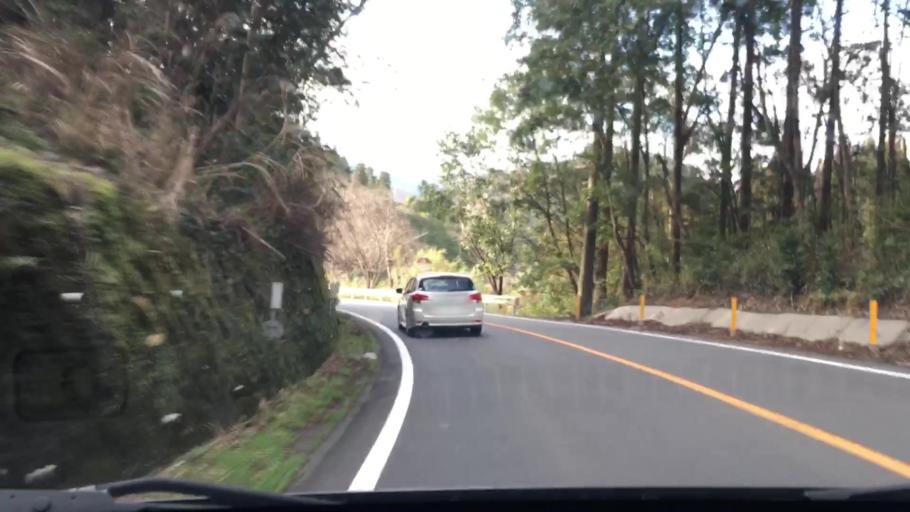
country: JP
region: Miyazaki
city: Nichinan
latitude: 31.7442
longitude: 131.3391
